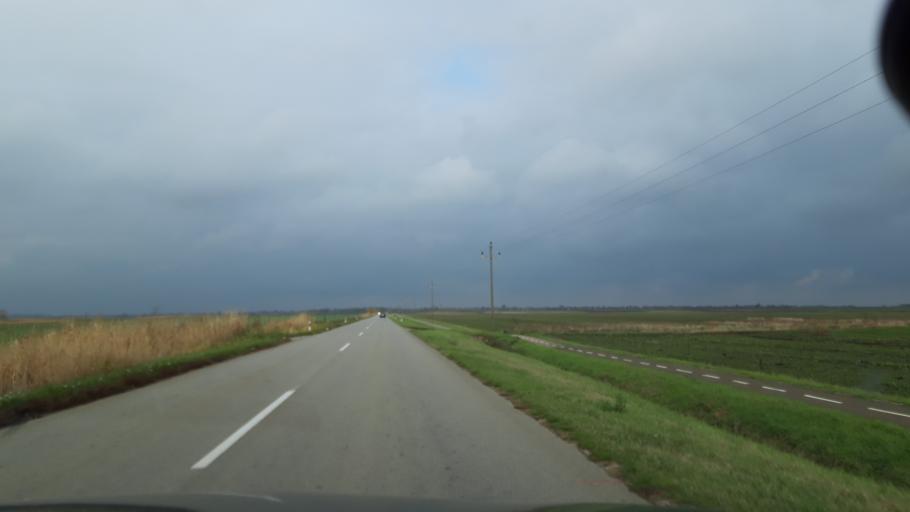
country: HU
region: Csongrad
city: Roszke
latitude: 46.1363
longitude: 20.0944
